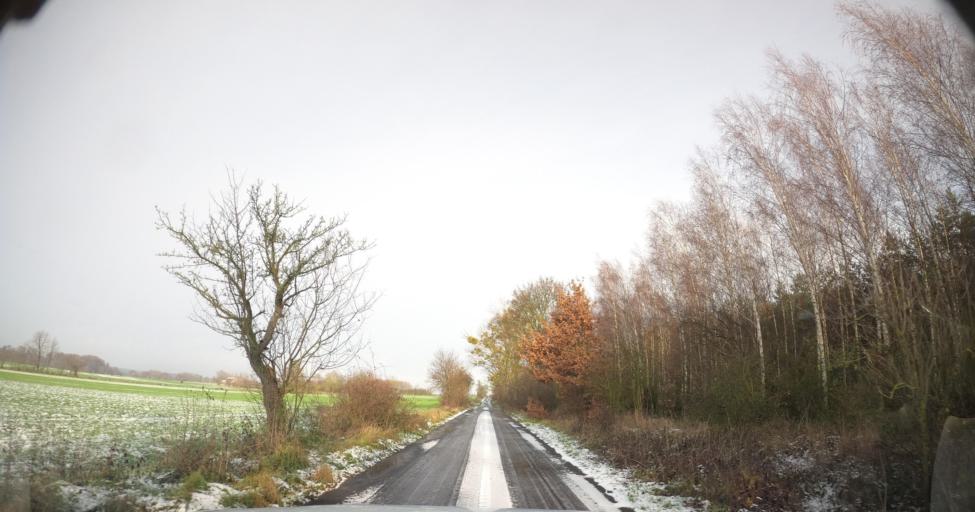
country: PL
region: West Pomeranian Voivodeship
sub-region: Powiat gryfinski
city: Mieszkowice
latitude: 52.7664
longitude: 14.4866
